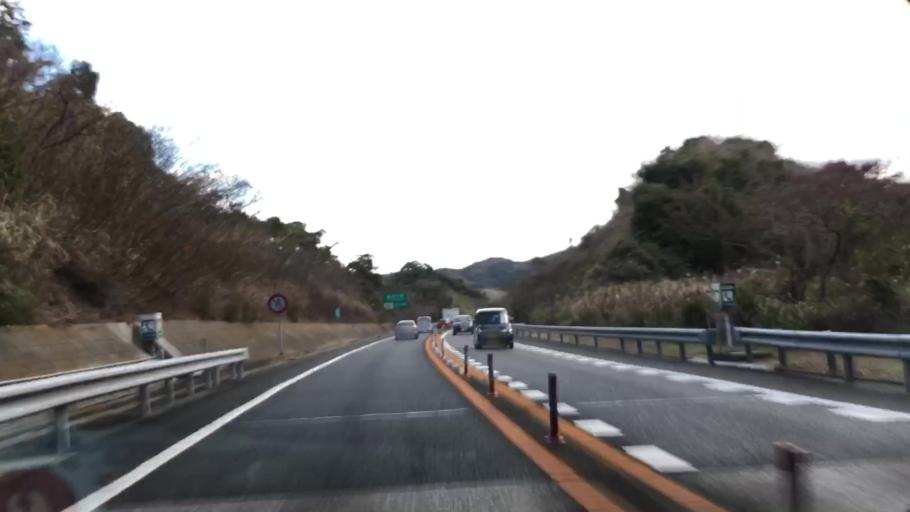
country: JP
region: Chiba
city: Futtsu
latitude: 35.1927
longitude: 139.8456
